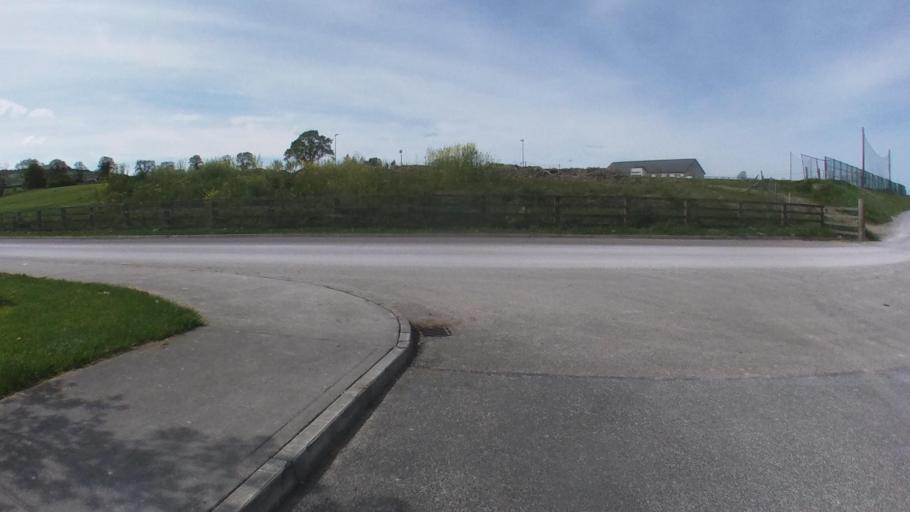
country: IE
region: Leinster
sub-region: County Carlow
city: Carlow
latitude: 52.8518
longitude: -6.9939
